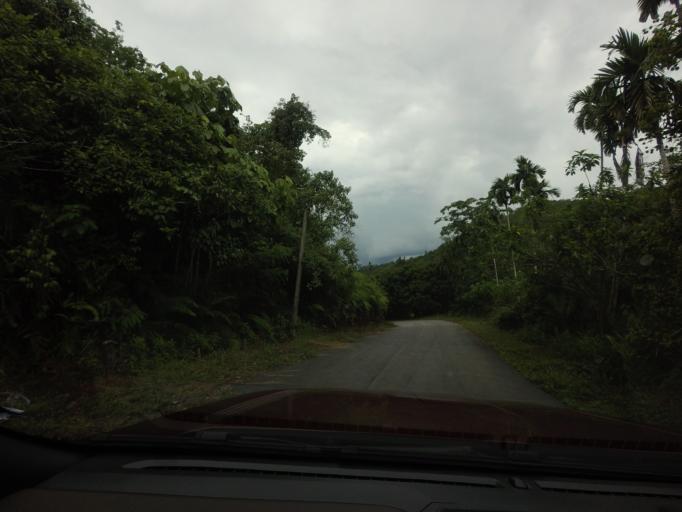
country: TH
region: Narathiwat
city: Sukhirin
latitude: 6.0004
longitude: 101.6976
